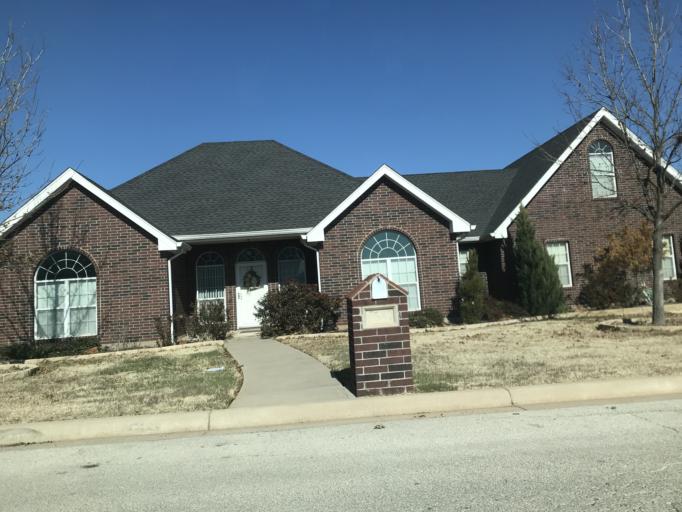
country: US
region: Texas
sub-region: Taylor County
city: Abilene
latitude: 32.3819
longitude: -99.7694
